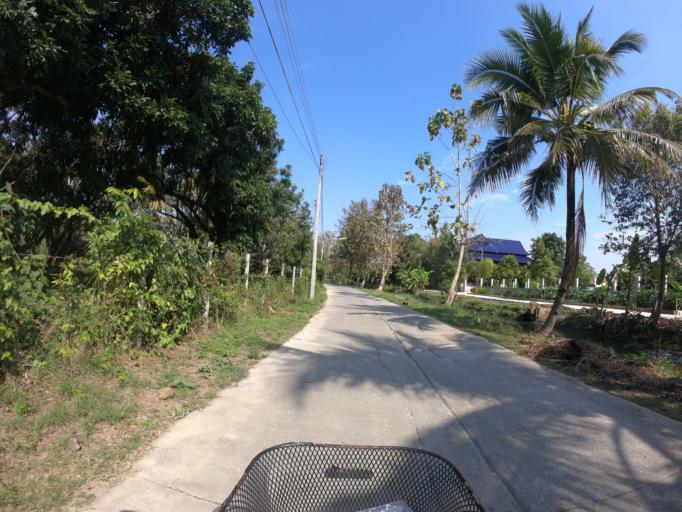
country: TH
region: Chiang Mai
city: Saraphi
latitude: 18.7063
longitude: 99.0596
